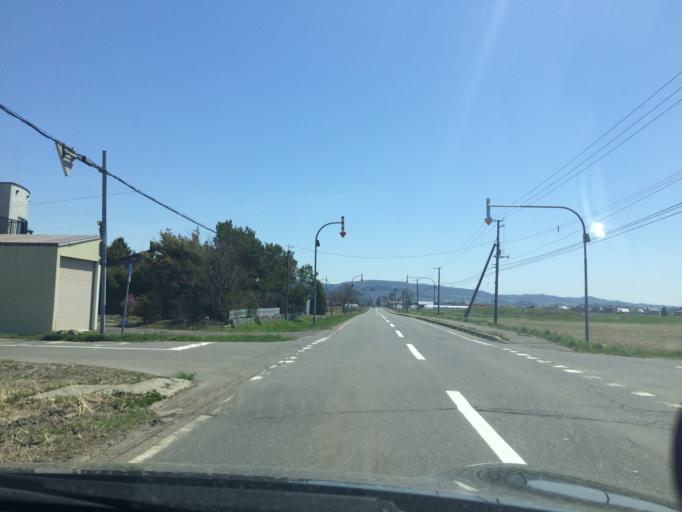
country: JP
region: Hokkaido
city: Kitahiroshima
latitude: 43.0172
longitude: 141.6740
